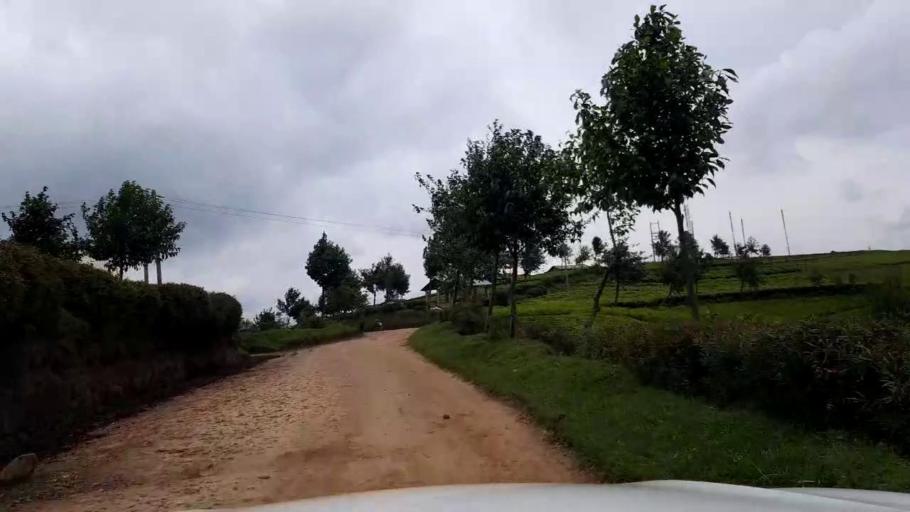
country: RW
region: Western Province
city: Kibuye
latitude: -1.9532
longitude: 29.4132
